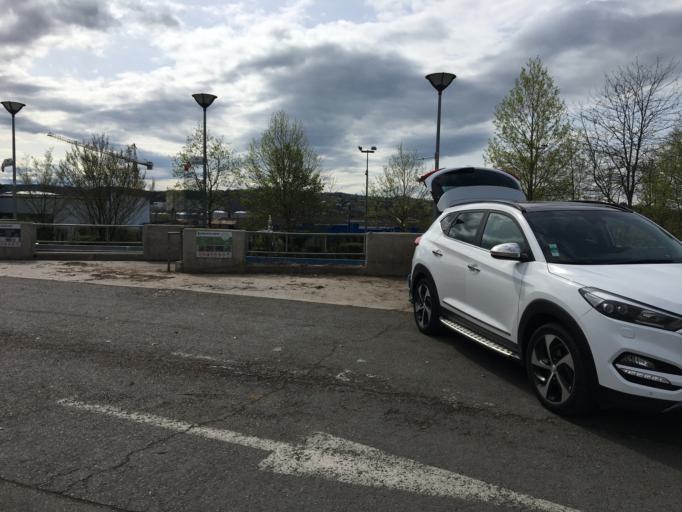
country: FR
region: Auvergne
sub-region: Departement de l'Allier
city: Cusset
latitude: 46.1427
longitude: 3.4500
